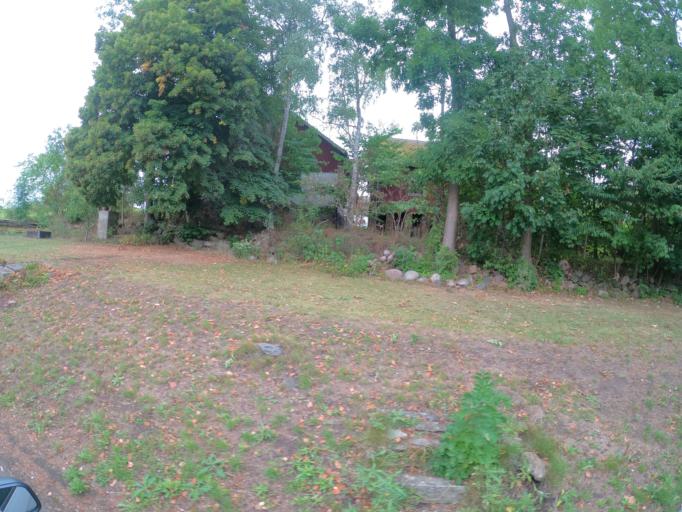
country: SE
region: Skane
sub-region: Lunds Kommun
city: Lund
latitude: 55.7738
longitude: 13.2265
